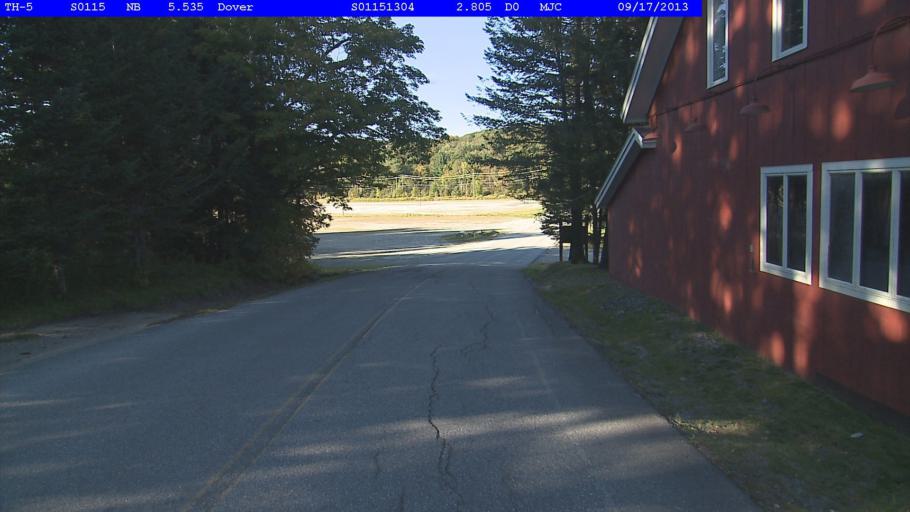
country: US
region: Vermont
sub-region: Windham County
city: Dover
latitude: 42.9646
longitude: -72.8902
